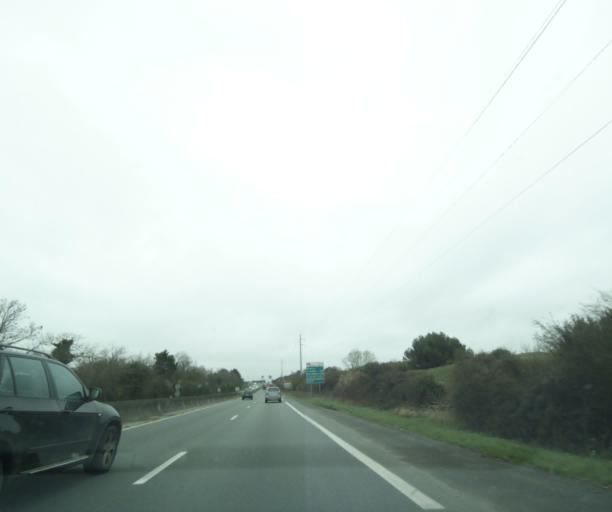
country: FR
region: Poitou-Charentes
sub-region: Departement de la Charente-Maritime
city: Puilboreau
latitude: 46.1654
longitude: -1.1216
